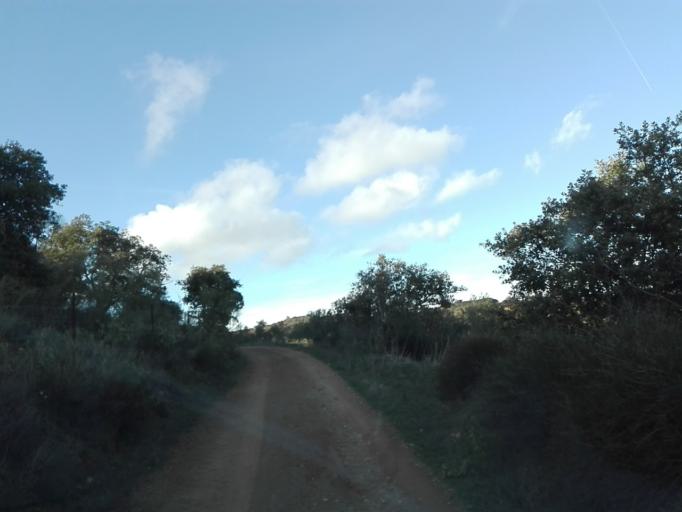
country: ES
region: Extremadura
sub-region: Provincia de Badajoz
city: Trasierra
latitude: 38.2054
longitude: -5.9991
